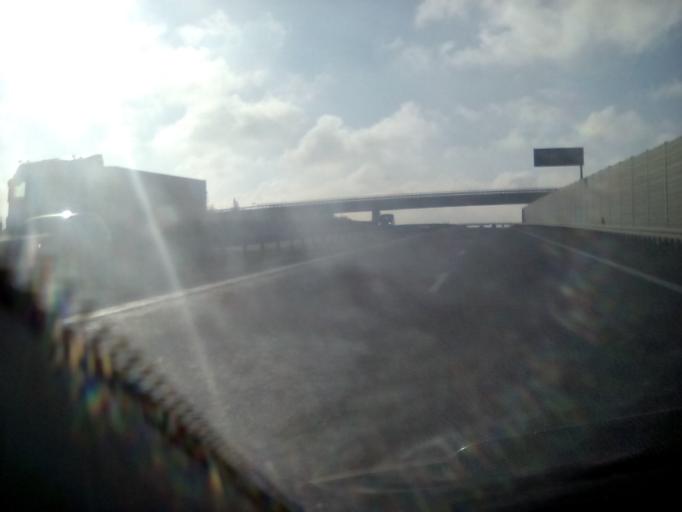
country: PL
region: Masovian Voivodeship
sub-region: Powiat grojecki
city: Jasieniec
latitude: 51.7881
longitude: 20.8933
